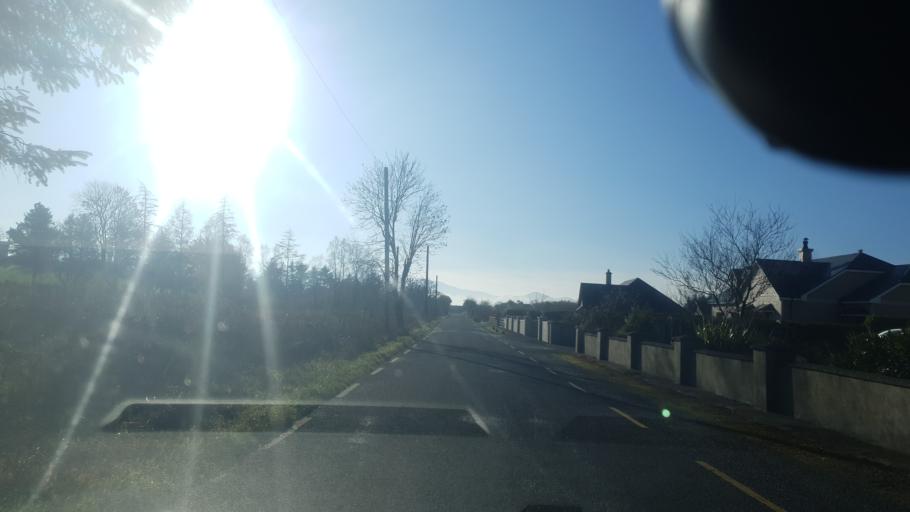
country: IE
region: Munster
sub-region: Ciarrai
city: Cill Airne
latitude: 52.1064
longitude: -9.4716
